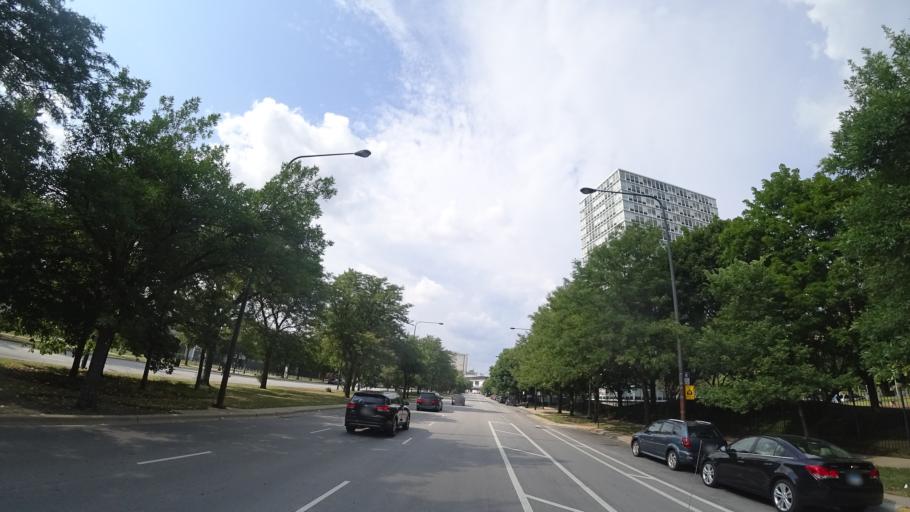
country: US
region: Illinois
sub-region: Cook County
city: Chicago
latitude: 41.8429
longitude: -87.6173
